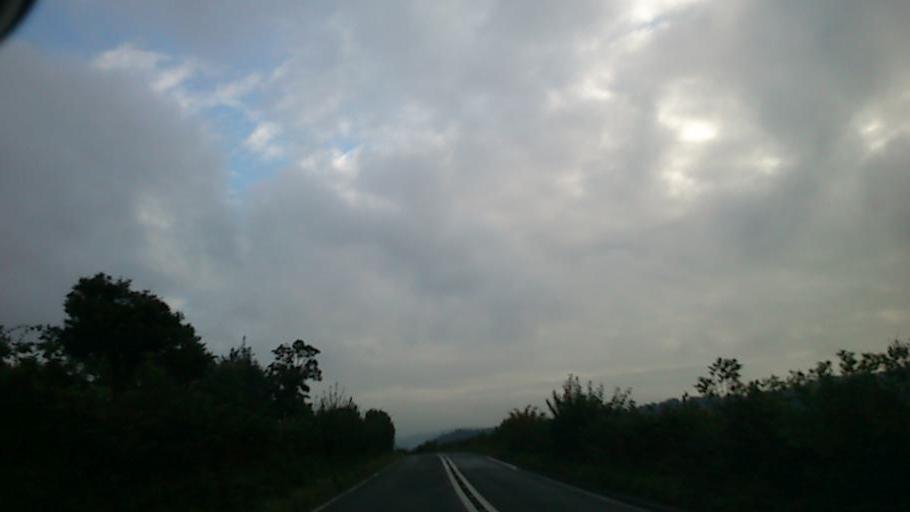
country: GB
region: Wales
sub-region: Sir Powys
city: Welshpool
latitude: 52.6502
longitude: -3.2066
